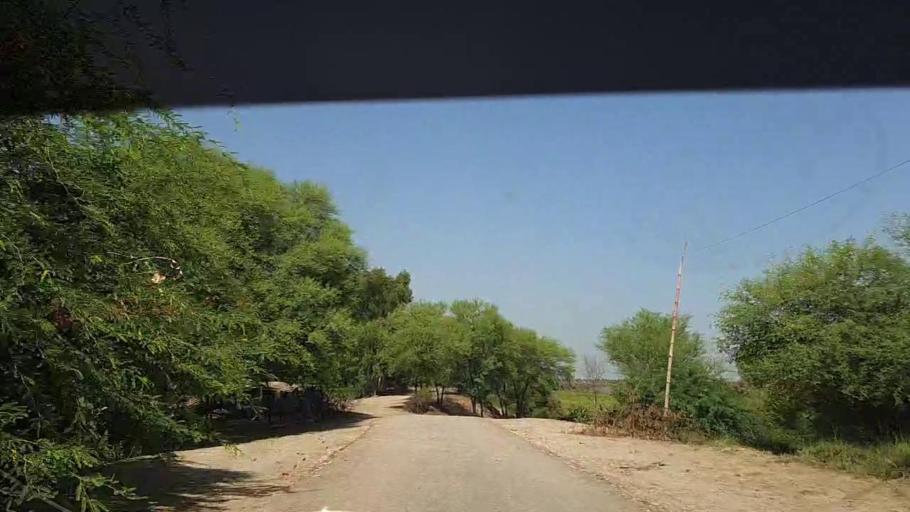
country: PK
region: Sindh
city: Ghauspur
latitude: 28.1692
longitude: 69.1425
